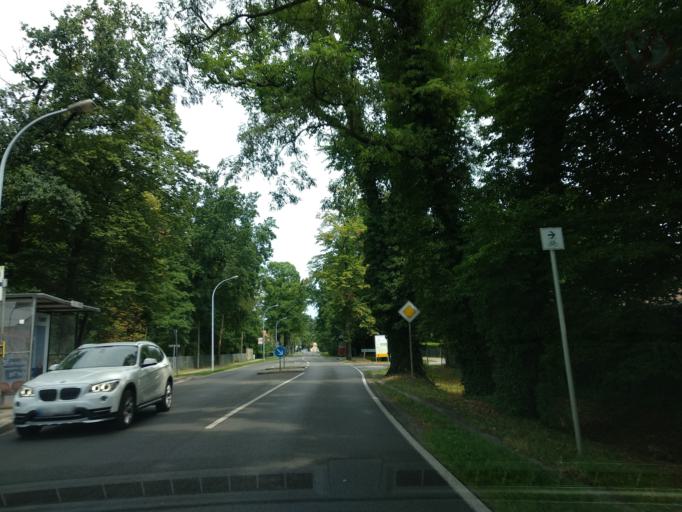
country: DE
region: Brandenburg
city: Leegebruch
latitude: 52.7520
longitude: 13.2034
